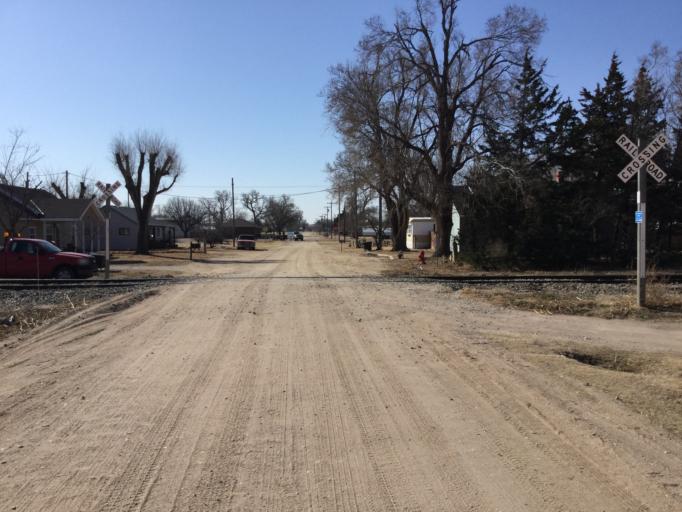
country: US
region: Kansas
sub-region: Rush County
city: La Crosse
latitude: 38.4671
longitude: -99.3116
